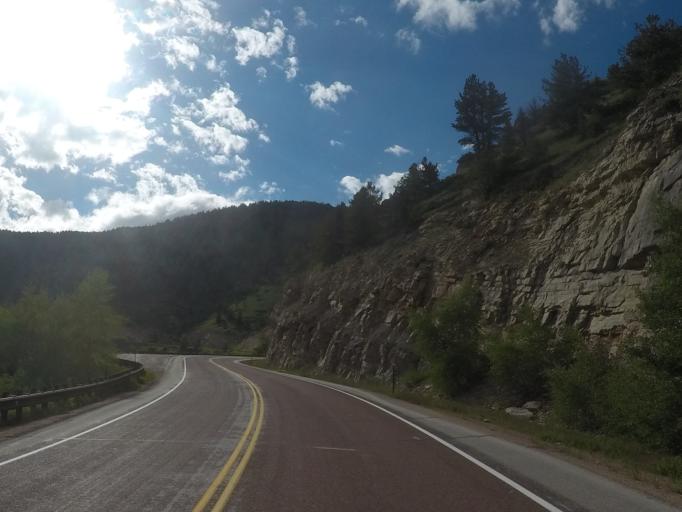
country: US
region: Wyoming
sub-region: Sheridan County
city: Sheridan
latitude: 44.8079
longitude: -107.3390
